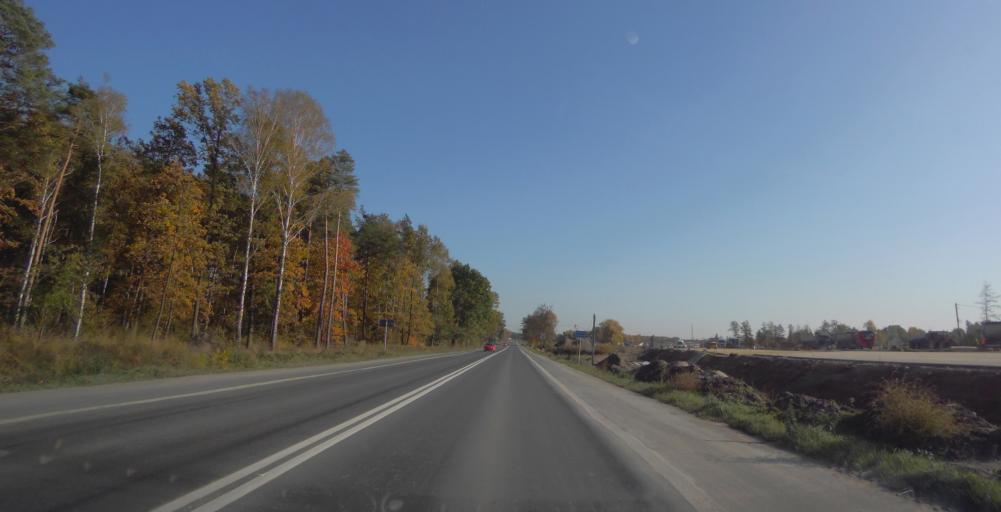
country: PL
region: Masovian Voivodeship
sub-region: Powiat otwocki
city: Kolbiel
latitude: 52.0811
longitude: 21.4383
